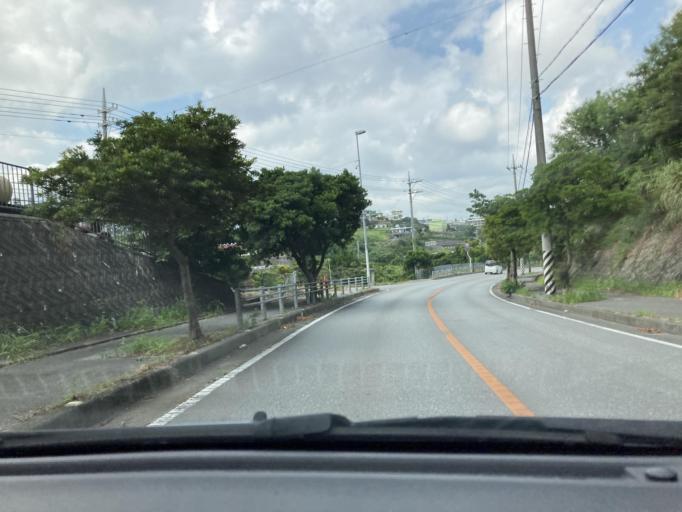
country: JP
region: Okinawa
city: Ginowan
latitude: 26.2634
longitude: 127.7747
